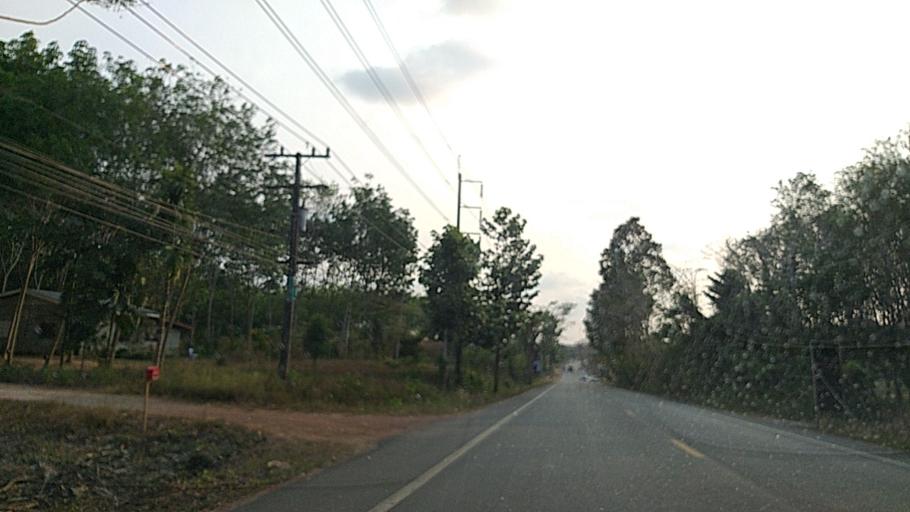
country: TH
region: Trat
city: Khao Saming
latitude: 12.3242
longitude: 102.3660
